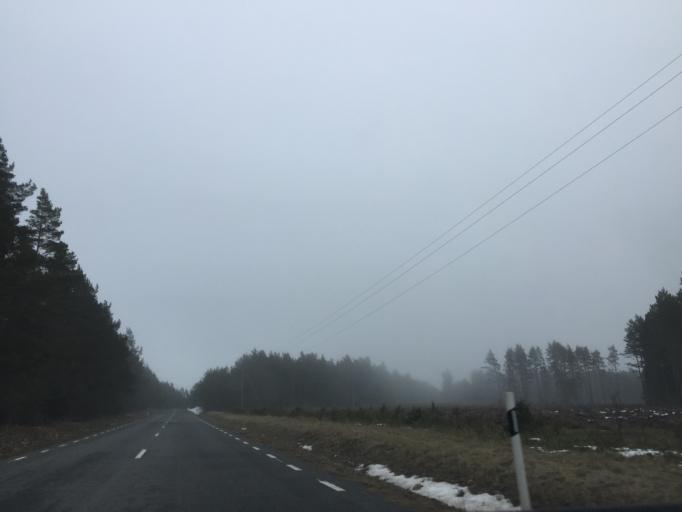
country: EE
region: Saare
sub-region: Kuressaare linn
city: Kuressaare
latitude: 58.4665
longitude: 22.0407
